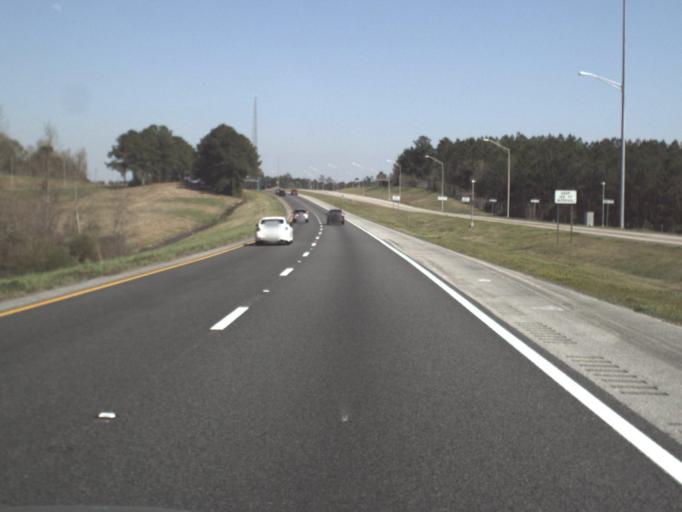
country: US
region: Florida
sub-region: Jackson County
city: Sneads
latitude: 30.6386
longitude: -84.9912
